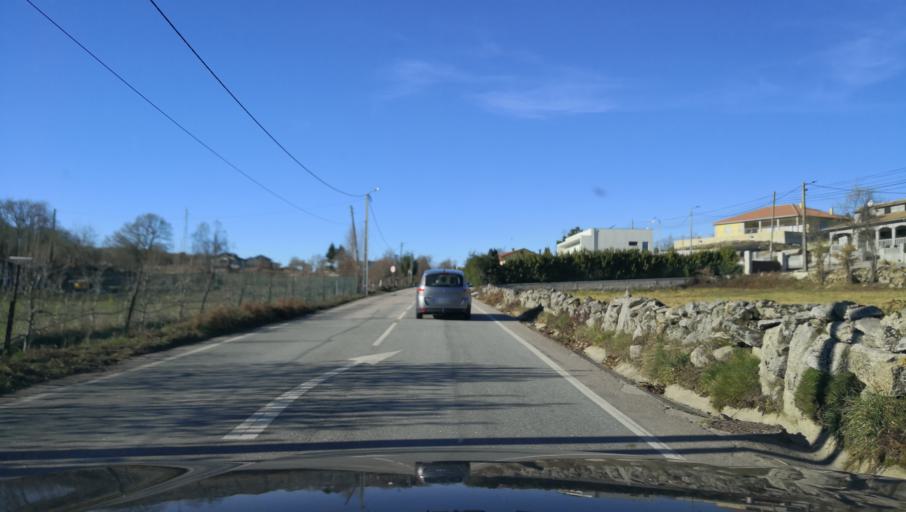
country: PT
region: Vila Real
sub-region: Vila Pouca de Aguiar
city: Vila Pouca de Aguiar
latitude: 41.4987
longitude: -7.6829
